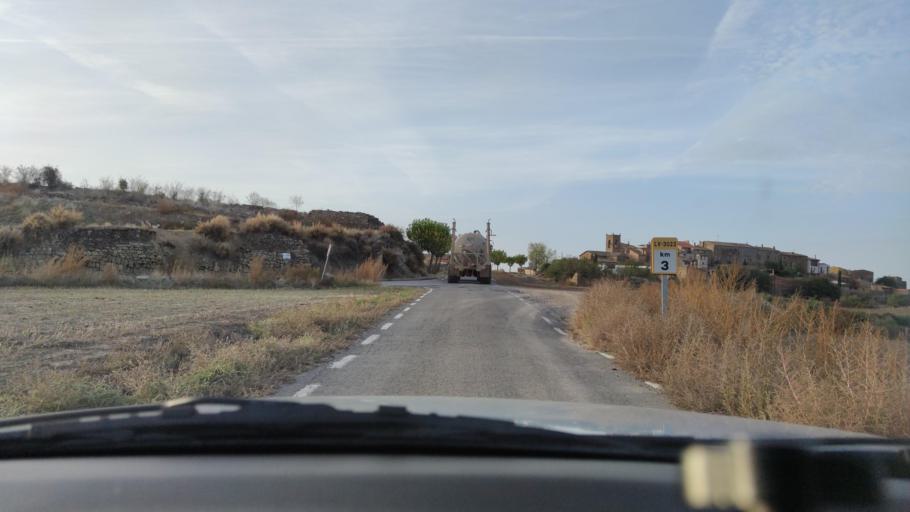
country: ES
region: Catalonia
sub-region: Provincia de Lleida
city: Agramunt
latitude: 41.8372
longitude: 1.0951
